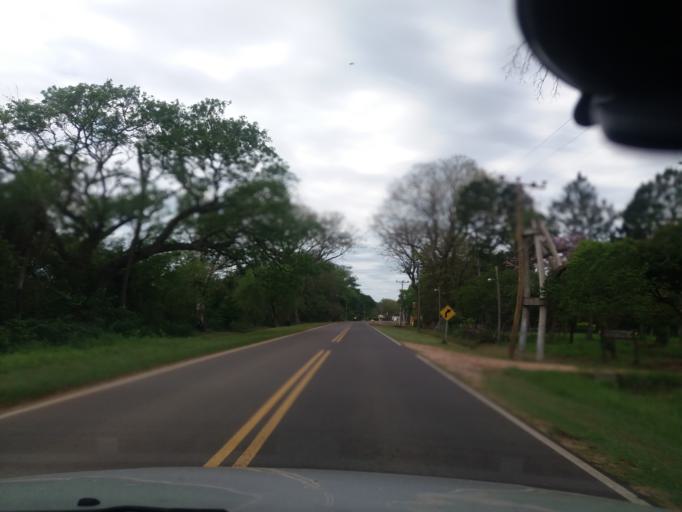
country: AR
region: Corrientes
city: San Luis del Palmar
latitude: -27.4568
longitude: -58.6782
